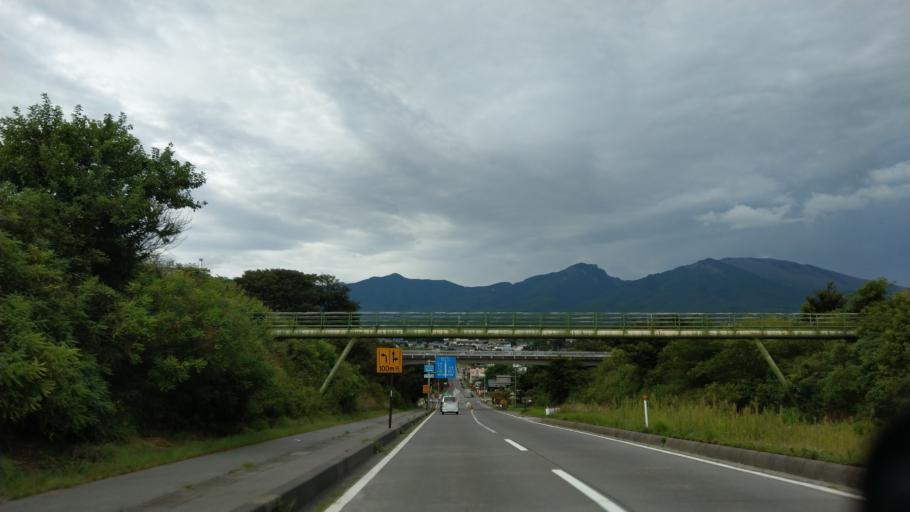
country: JP
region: Nagano
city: Komoro
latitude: 36.3104
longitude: 138.4566
